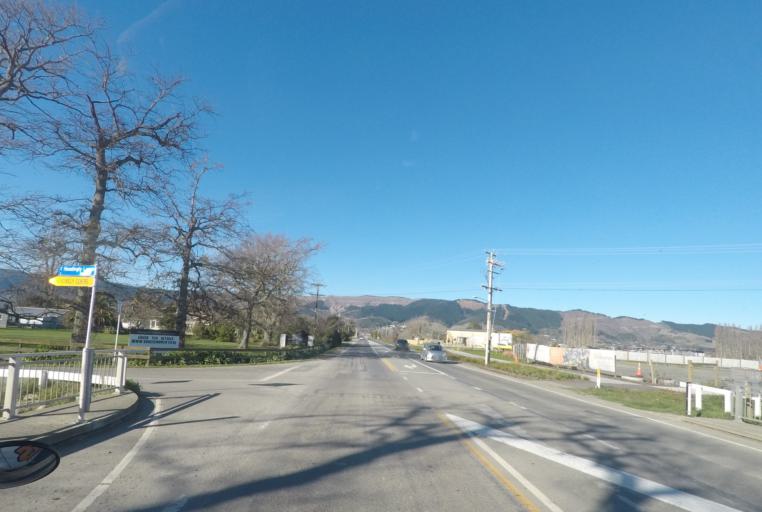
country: NZ
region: Tasman
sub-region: Tasman District
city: Richmond
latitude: -41.3276
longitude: 173.1719
